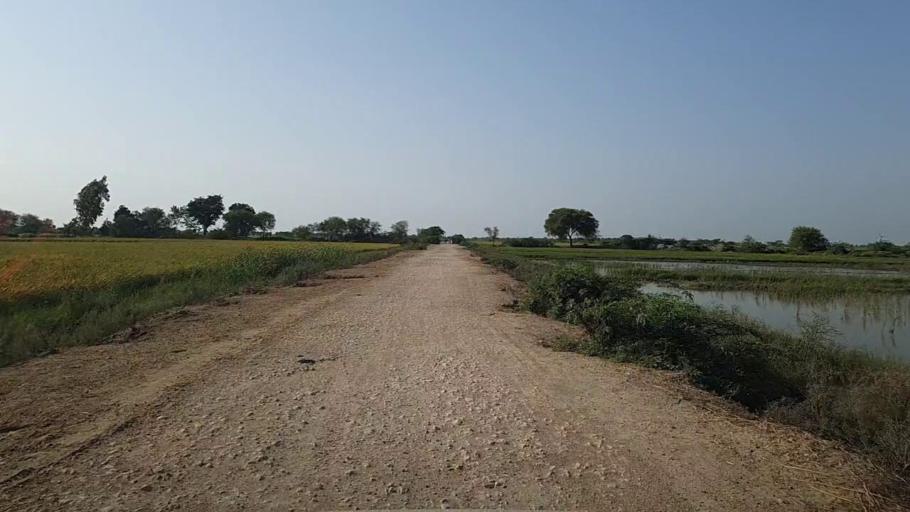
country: PK
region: Sindh
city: Kario
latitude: 24.8060
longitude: 68.5108
